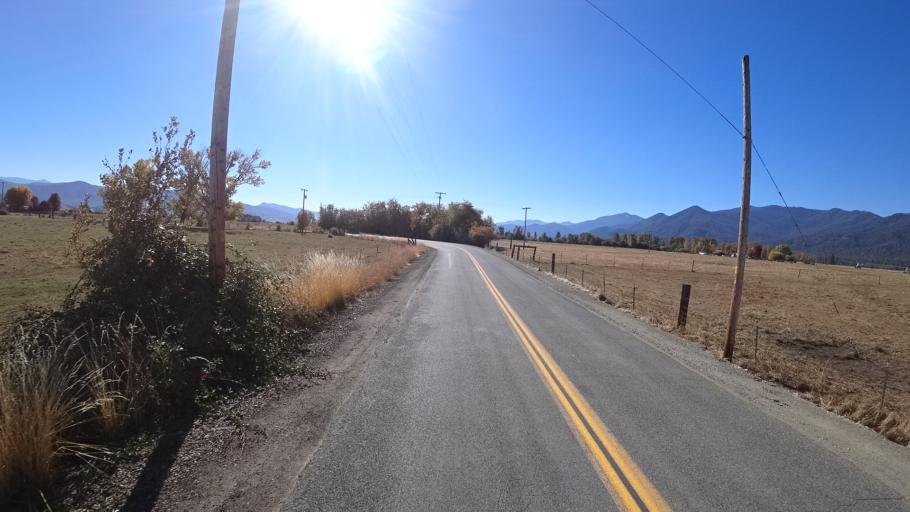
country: US
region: California
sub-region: Siskiyou County
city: Yreka
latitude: 41.5137
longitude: -122.8882
